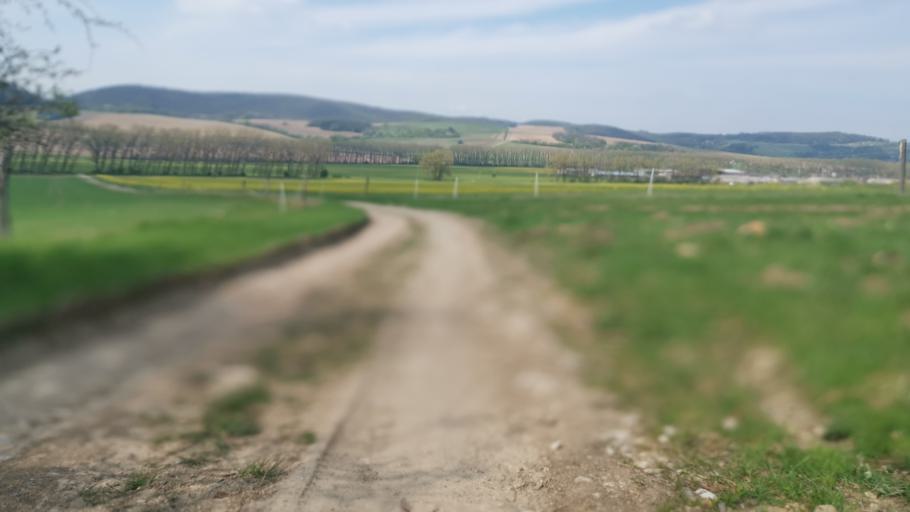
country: SK
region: Trnavsky
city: Smolenice
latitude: 48.5328
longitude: 17.3818
